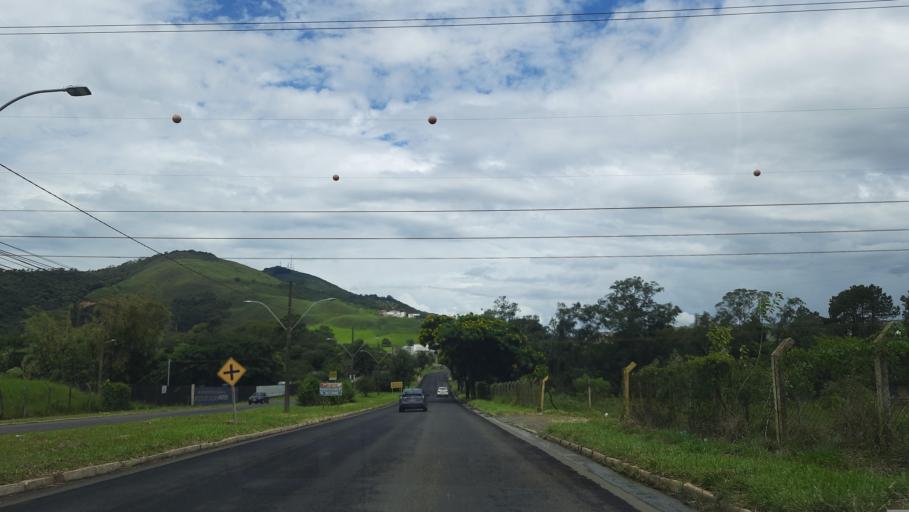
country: BR
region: Minas Gerais
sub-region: Pocos De Caldas
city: Pocos de Caldas
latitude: -21.7754
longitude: -46.6092
